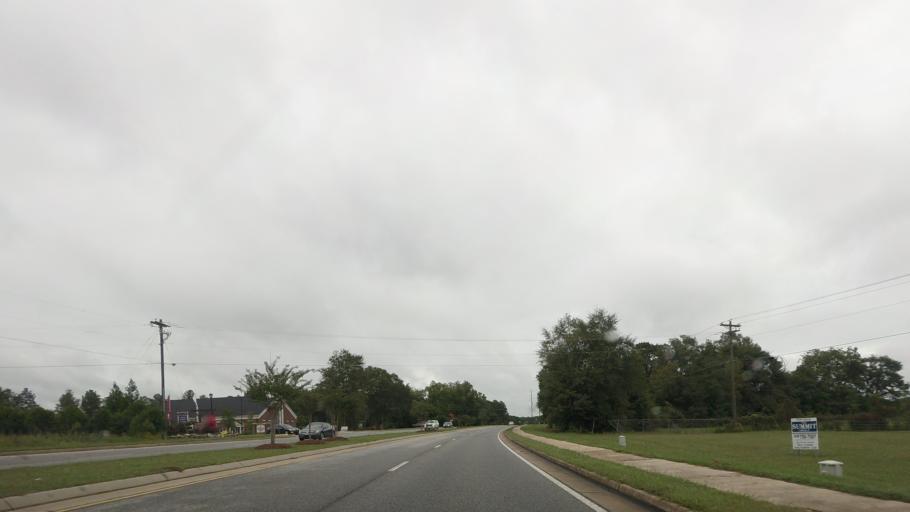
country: US
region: Georgia
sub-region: Houston County
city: Perry
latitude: 32.5303
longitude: -83.6622
